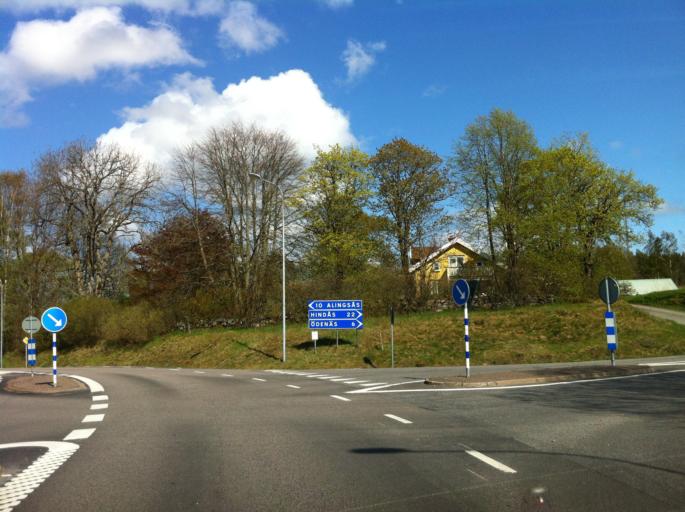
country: SE
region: Vaestra Goetaland
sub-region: Alingsas Kommun
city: Alingsas
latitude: 57.8580
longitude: 12.5578
